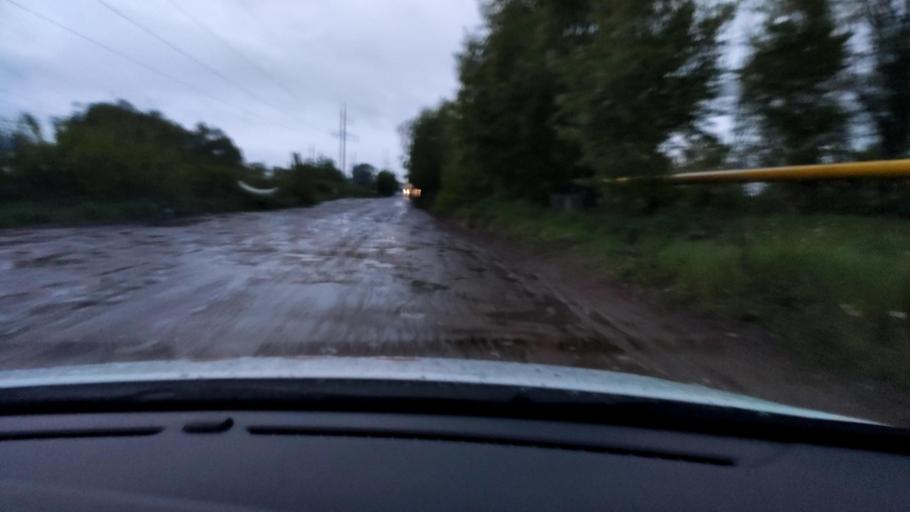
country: RU
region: Tatarstan
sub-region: Gorod Kazan'
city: Kazan
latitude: 55.7226
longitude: 49.1256
